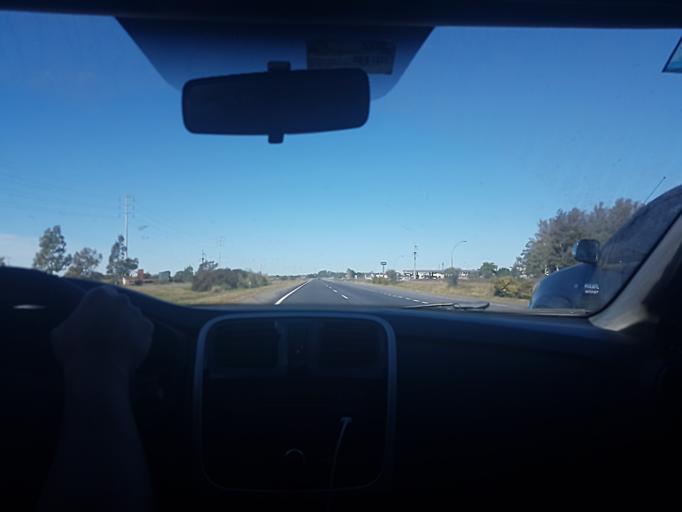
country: AR
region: Cordoba
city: Pilar
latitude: -31.6487
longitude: -63.8588
